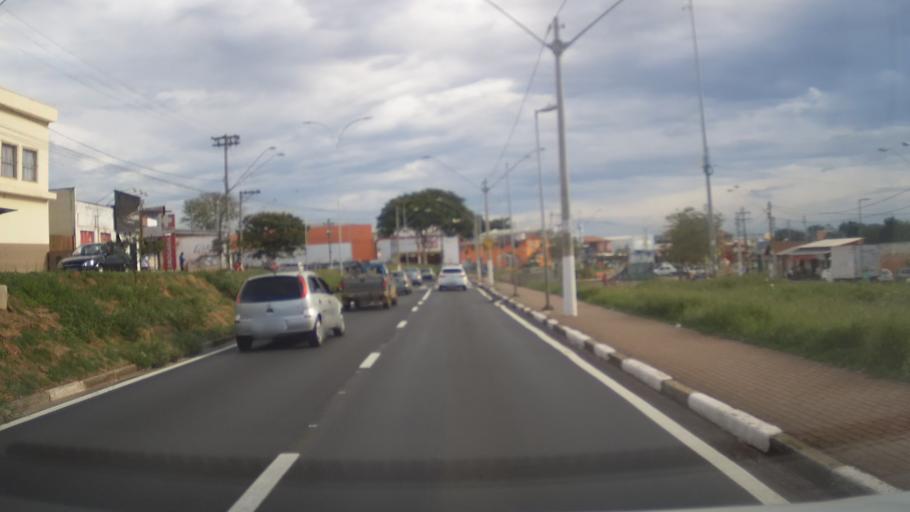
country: BR
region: Sao Paulo
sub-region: Hortolandia
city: Hortolandia
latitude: -22.9494
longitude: -47.1866
